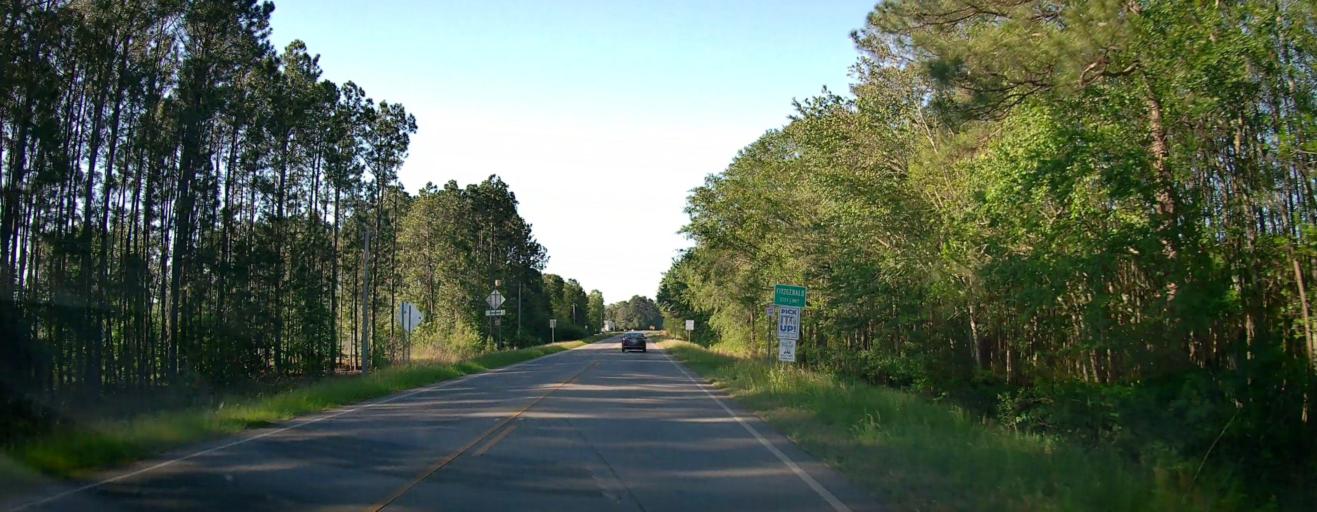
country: US
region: Georgia
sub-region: Ben Hill County
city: Fitzgerald
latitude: 31.6989
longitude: -83.2393
